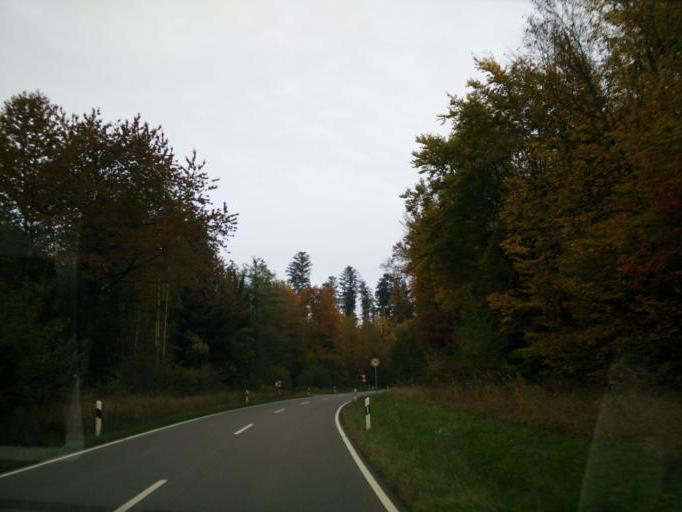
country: DE
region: Baden-Wuerttemberg
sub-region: Tuebingen Region
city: Dettenhausen
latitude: 48.5906
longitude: 9.0750
